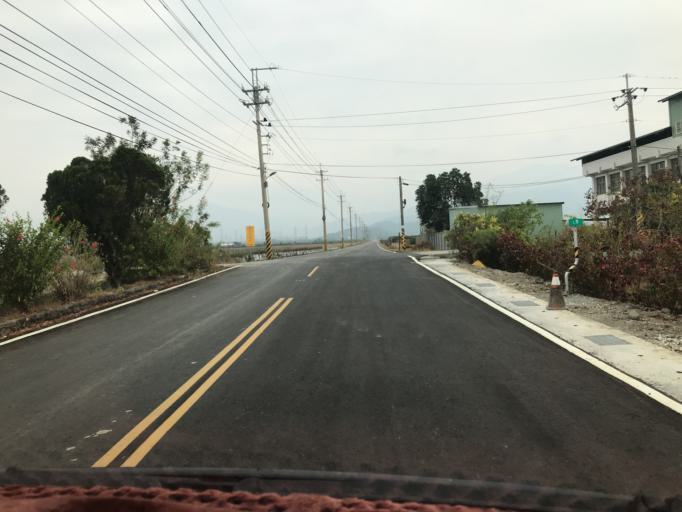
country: TW
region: Taiwan
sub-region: Pingtung
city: Pingtung
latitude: 22.4098
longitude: 120.5953
